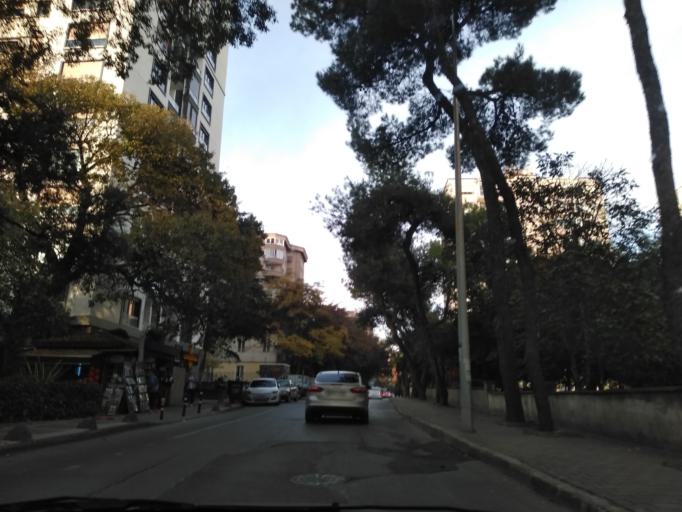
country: TR
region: Istanbul
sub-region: Atasehir
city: Atasehir
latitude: 40.9715
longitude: 29.0910
